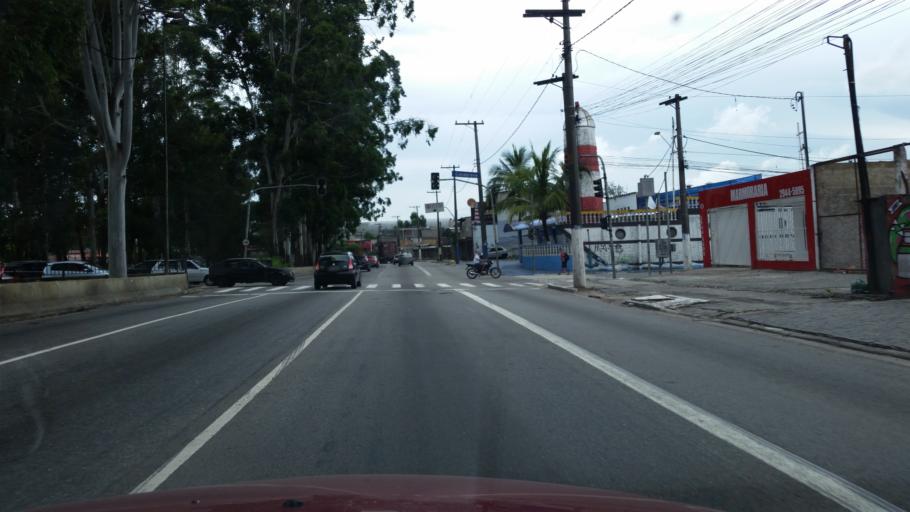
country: BR
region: Sao Paulo
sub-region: Ferraz De Vasconcelos
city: Ferraz de Vasconcelos
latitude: -23.5459
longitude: -46.4468
